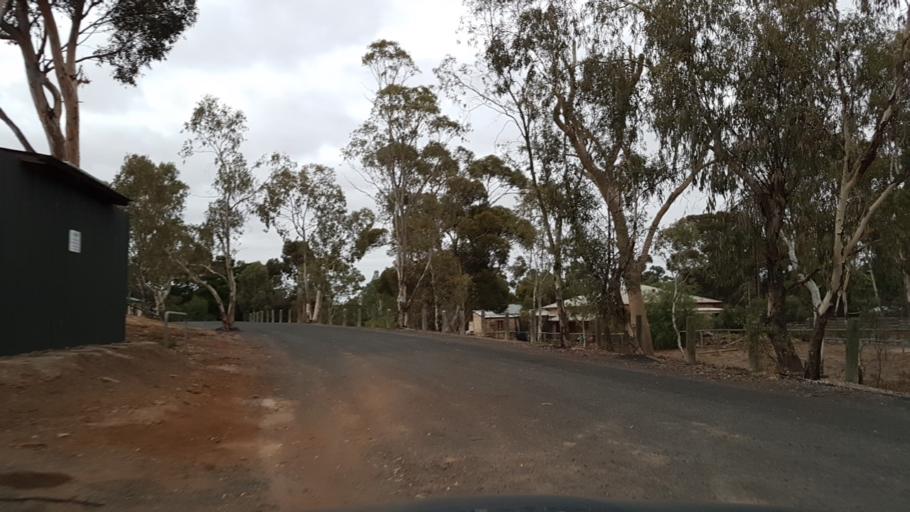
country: AU
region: South Australia
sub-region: Mount Barker
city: Callington
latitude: -35.0689
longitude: 139.0138
